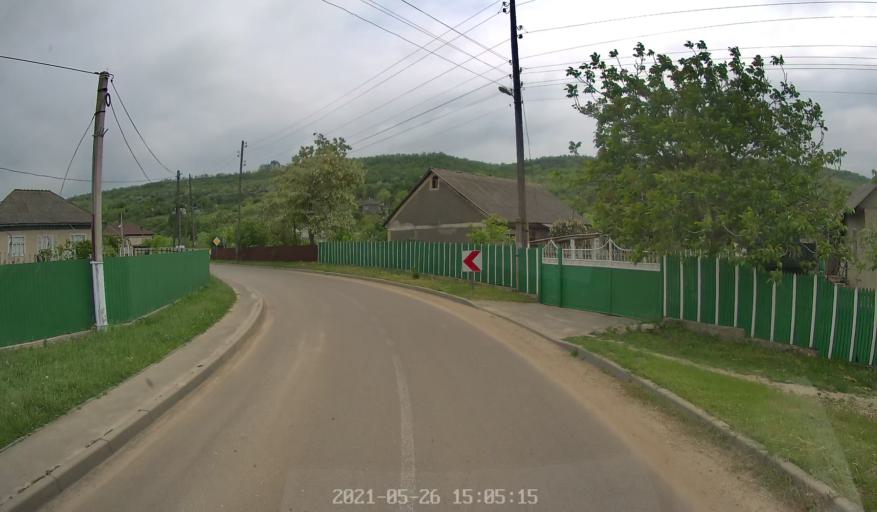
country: MD
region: Hincesti
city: Dancu
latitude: 46.6643
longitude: 28.3287
